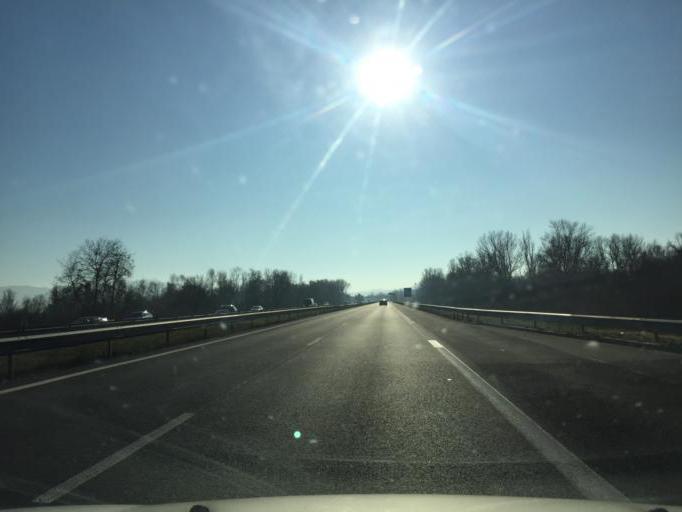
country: FR
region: Rhone-Alpes
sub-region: Departement du Rhone
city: Anse
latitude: 45.9114
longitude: 4.7272
